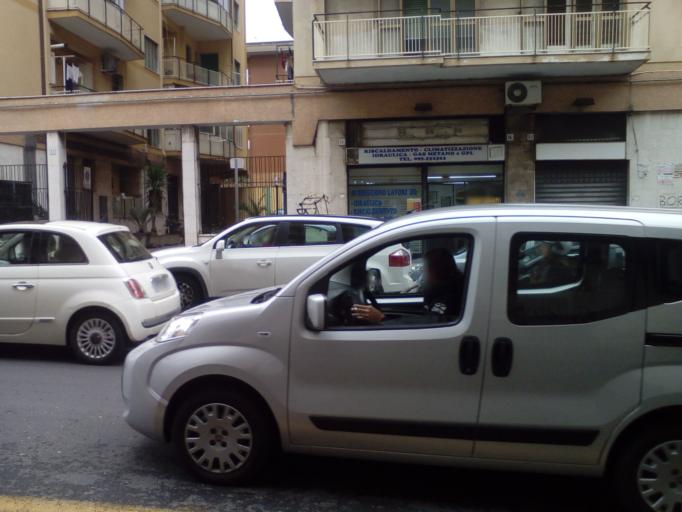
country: IT
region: Sicily
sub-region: Catania
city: Catania
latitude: 37.5156
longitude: 15.0779
